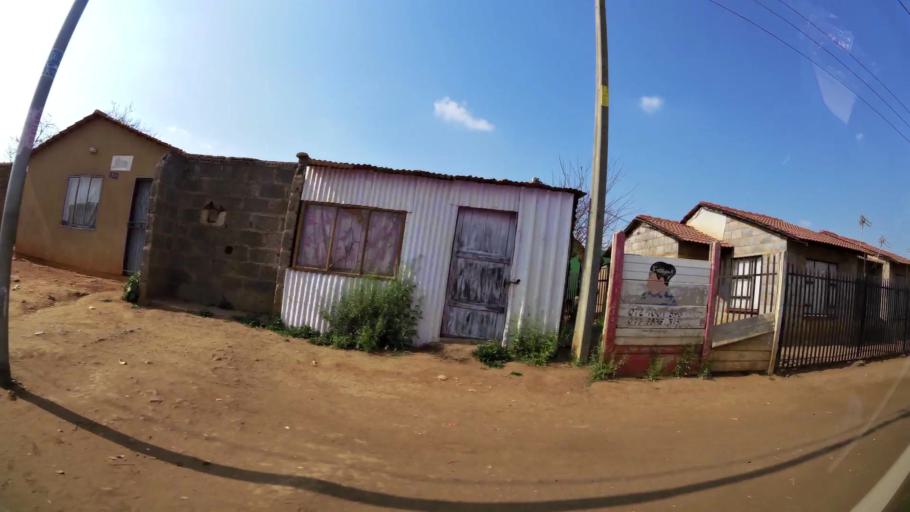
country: ZA
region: Gauteng
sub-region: Ekurhuleni Metropolitan Municipality
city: Springs
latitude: -26.1186
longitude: 28.4841
